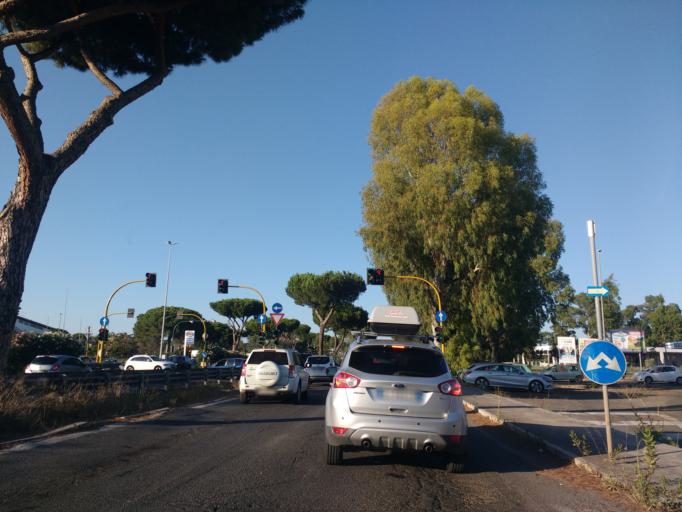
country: IT
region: Latium
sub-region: Citta metropolitana di Roma Capitale
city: Acilia-Castel Fusano-Ostia Antica
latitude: 41.7545
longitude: 12.3695
